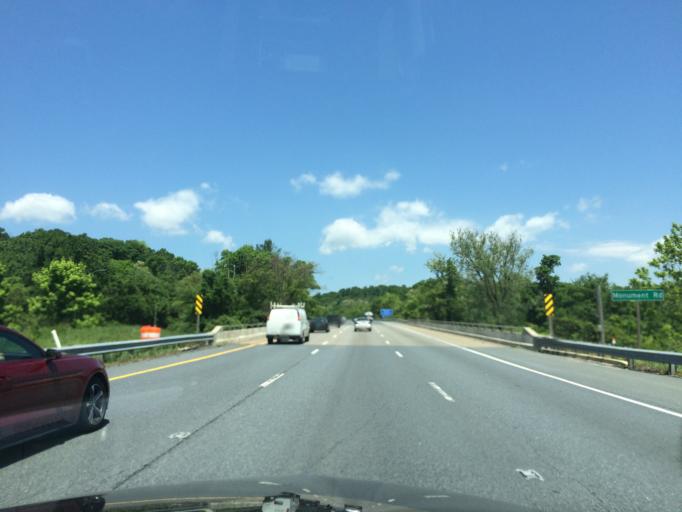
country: US
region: Maryland
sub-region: Frederick County
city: Myersville
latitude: 39.5138
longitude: -77.5944
